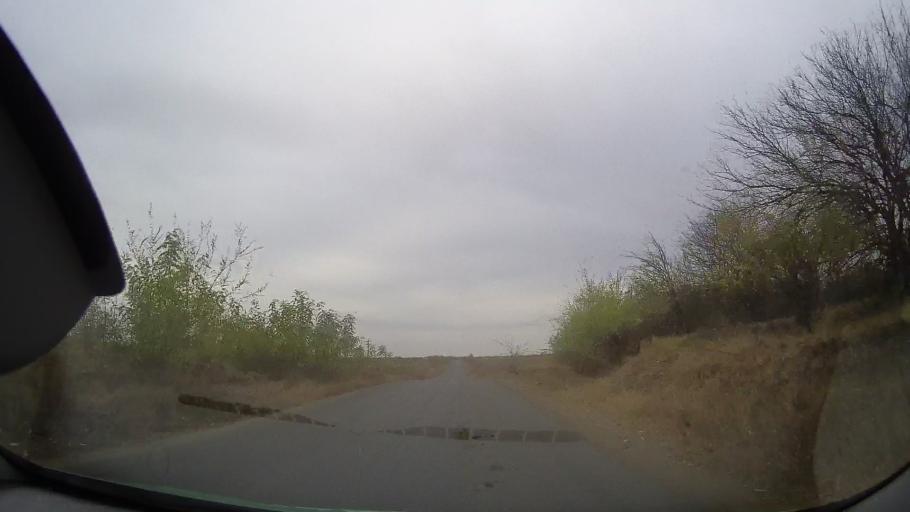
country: RO
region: Buzau
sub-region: Comuna Largu
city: Largu
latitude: 44.9729
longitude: 27.1675
